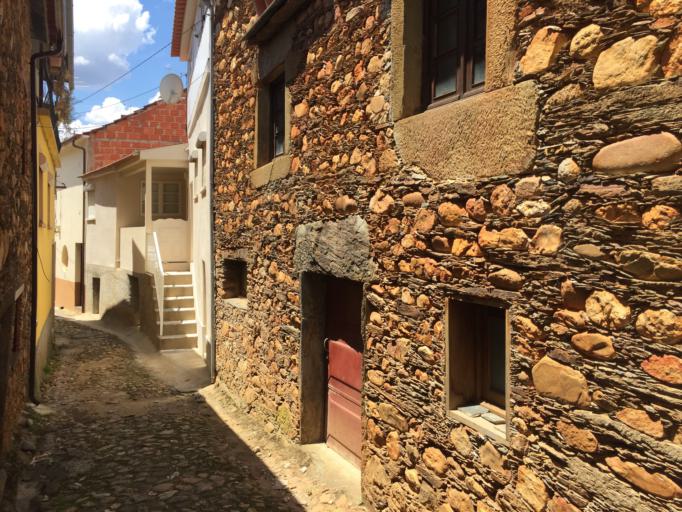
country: PT
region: Coimbra
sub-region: Pampilhosa da Serra
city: Pampilhosa da Serra
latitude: 40.0670
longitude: -7.8005
